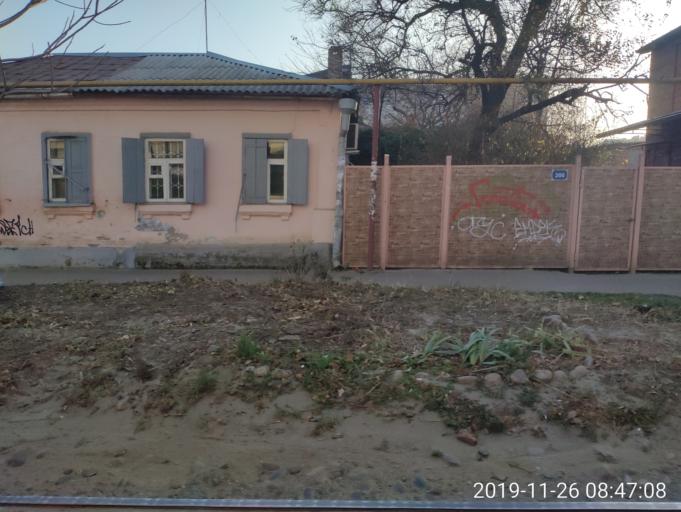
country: RU
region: Krasnodarskiy
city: Krasnodar
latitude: 45.0386
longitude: 38.9796
